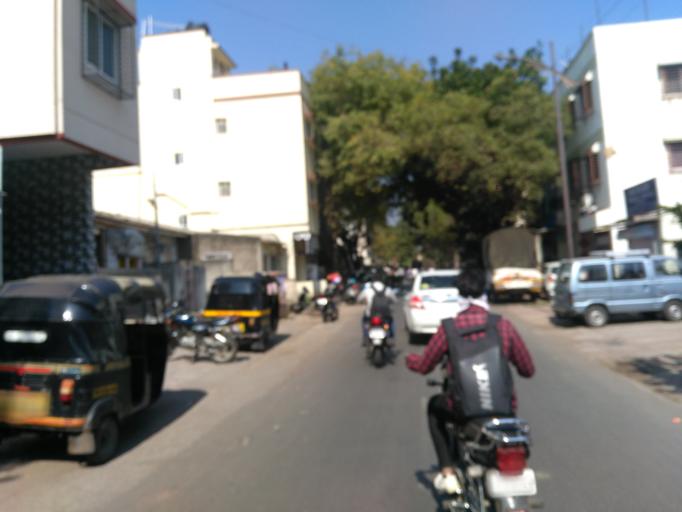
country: IN
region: Maharashtra
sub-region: Pune Division
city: Pune
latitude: 18.4931
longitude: 73.8486
